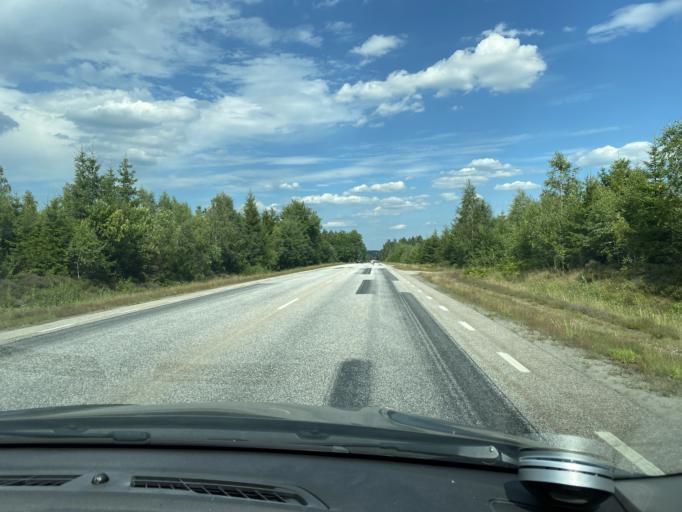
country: SE
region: Kronoberg
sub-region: Markaryds Kommun
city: Markaryd
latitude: 56.4282
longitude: 13.5605
